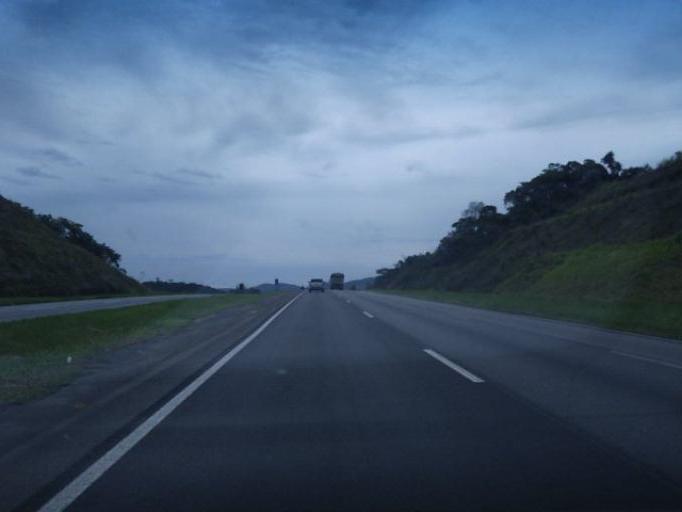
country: BR
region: Sao Paulo
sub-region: Juquia
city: Juquia
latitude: -24.3316
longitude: -47.6096
